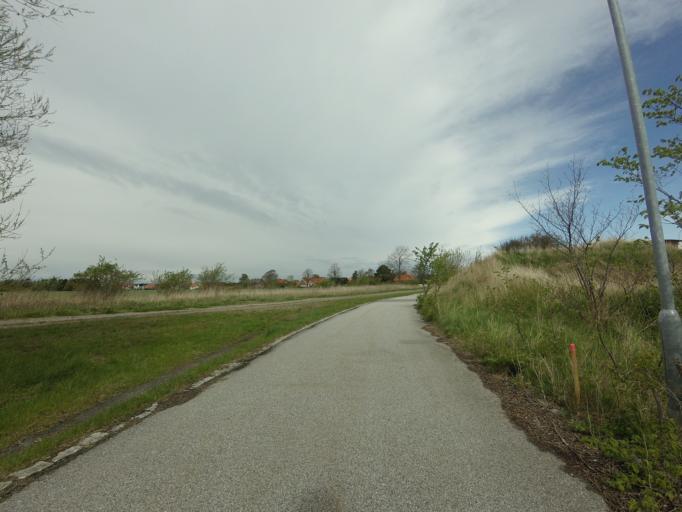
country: SE
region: Skane
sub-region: Malmo
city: Bunkeflostrand
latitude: 55.5501
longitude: 12.9665
